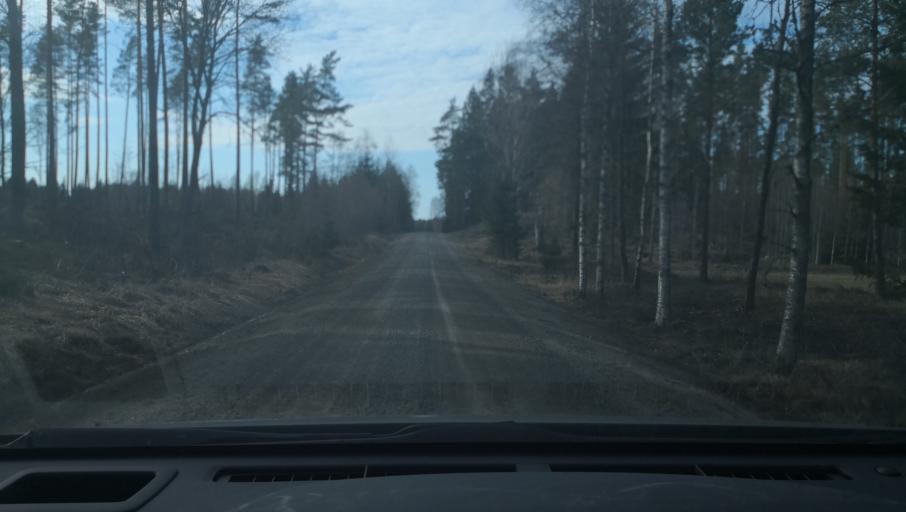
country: SE
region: Uppsala
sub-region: Heby Kommun
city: Heby
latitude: 59.8497
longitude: 16.8826
